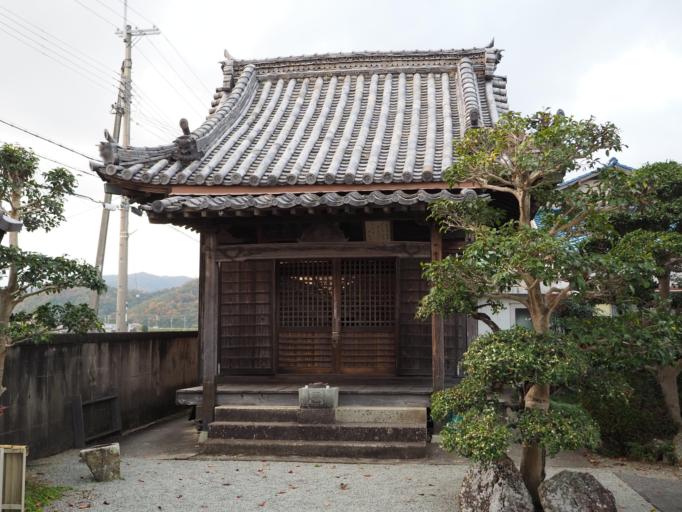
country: JP
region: Hyogo
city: Himeji
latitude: 34.9553
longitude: 134.7723
